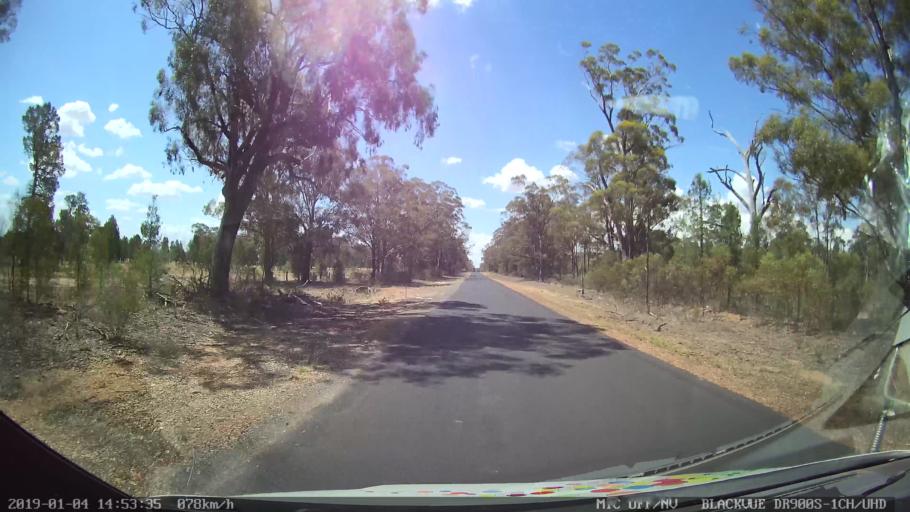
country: AU
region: New South Wales
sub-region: Dubbo Municipality
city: Dubbo
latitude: -32.0015
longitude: 148.6522
